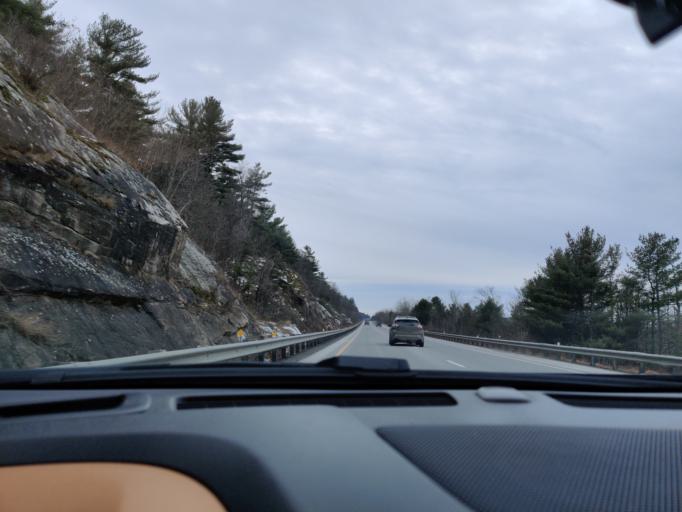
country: US
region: New York
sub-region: Jefferson County
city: Alexandria Bay
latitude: 44.4127
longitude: -75.9245
